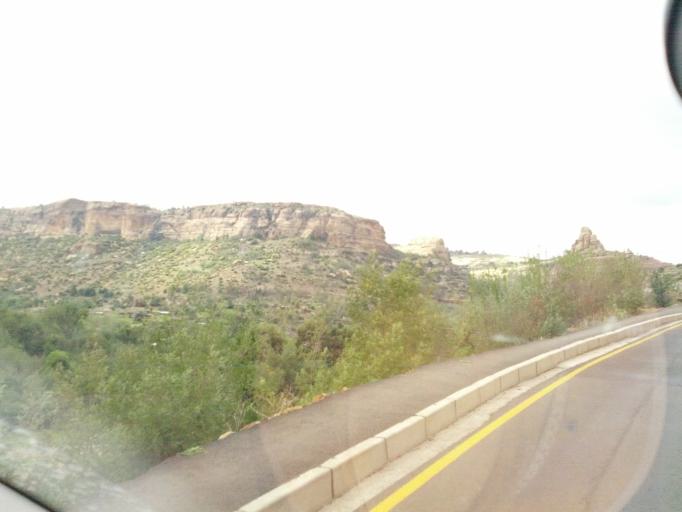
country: LS
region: Maseru
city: Nako
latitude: -29.4742
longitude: 27.7394
